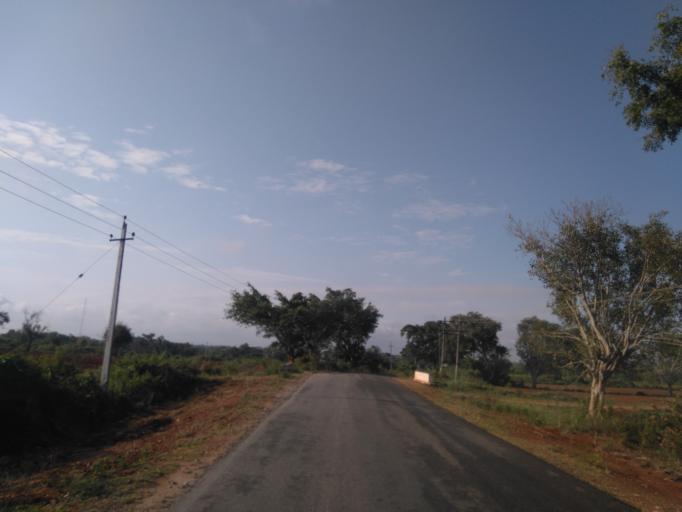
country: IN
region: Karnataka
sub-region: Mandya
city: Malavalli
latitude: 12.3078
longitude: 77.0726
